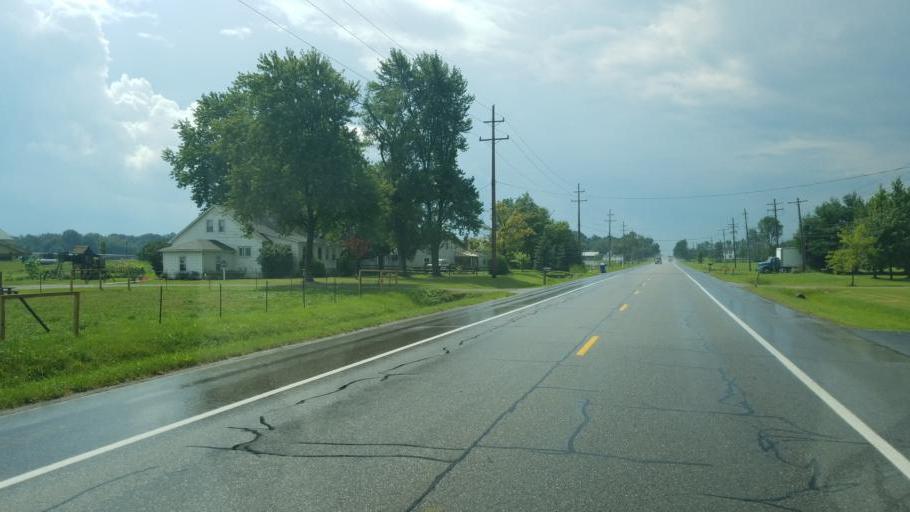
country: US
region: Ohio
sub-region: Geauga County
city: Middlefield
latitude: 41.4736
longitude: -81.0513
